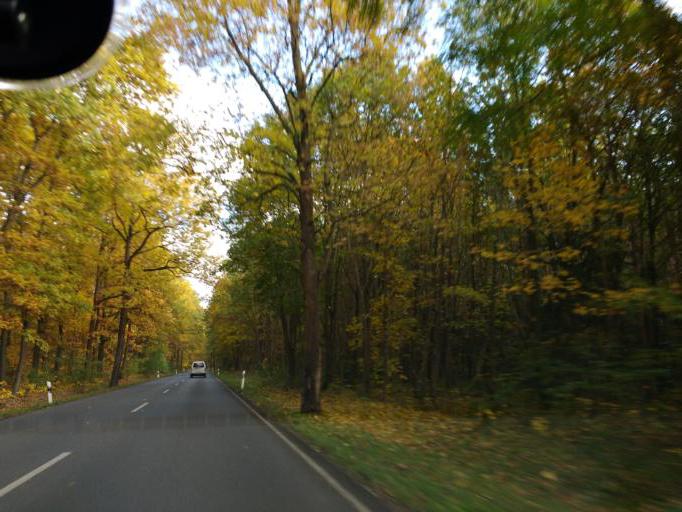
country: DE
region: Brandenburg
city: Petershagen
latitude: 52.5574
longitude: 13.7985
